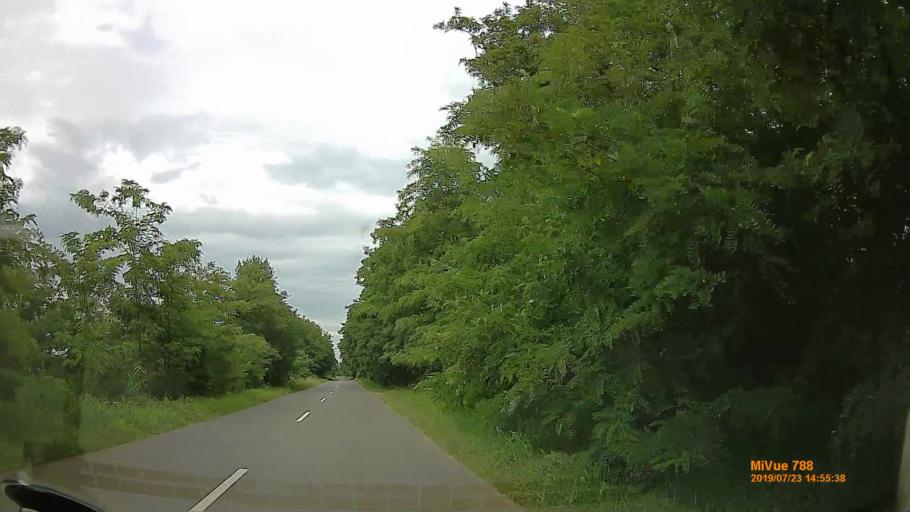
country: HU
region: Szabolcs-Szatmar-Bereg
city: Kalmanhaza
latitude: 47.8928
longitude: 21.6602
